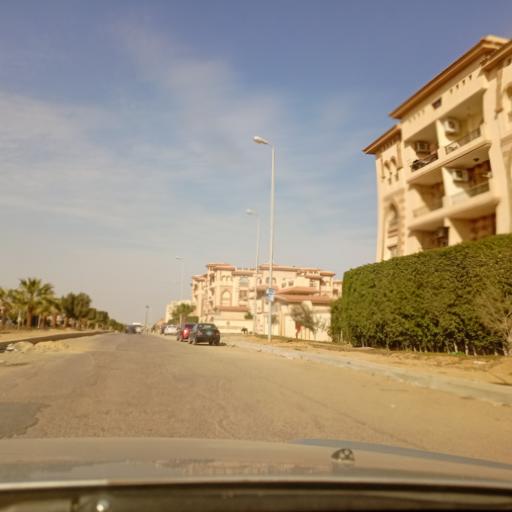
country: EG
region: Muhafazat al Qalyubiyah
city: Al Khankah
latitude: 30.0474
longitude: 31.4852
